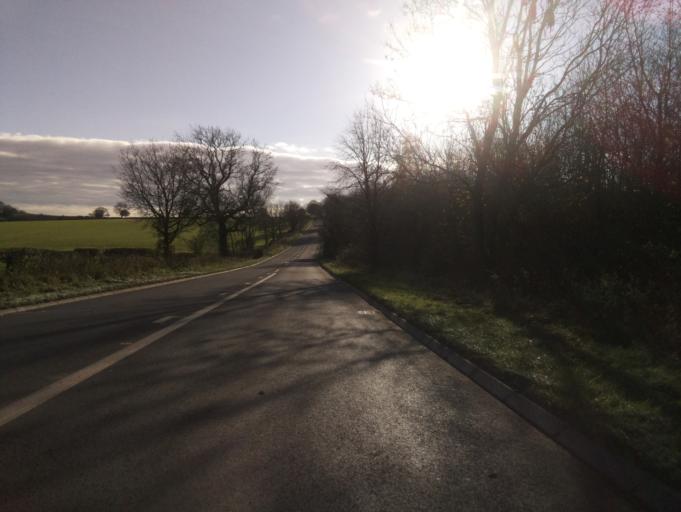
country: GB
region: England
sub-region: Staffordshire
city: Barton under Needwood
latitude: 52.8405
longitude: -1.7786
